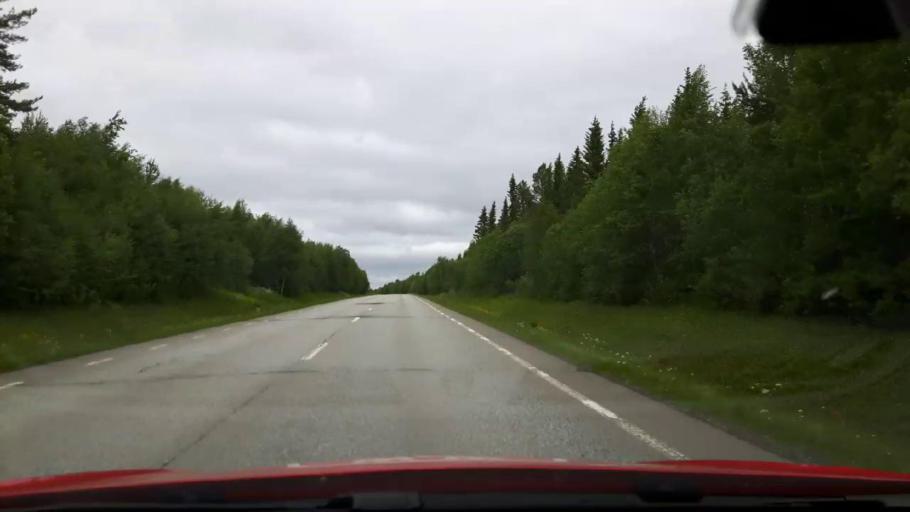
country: SE
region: Jaemtland
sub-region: OEstersunds Kommun
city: Lit
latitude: 63.6158
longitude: 14.6751
